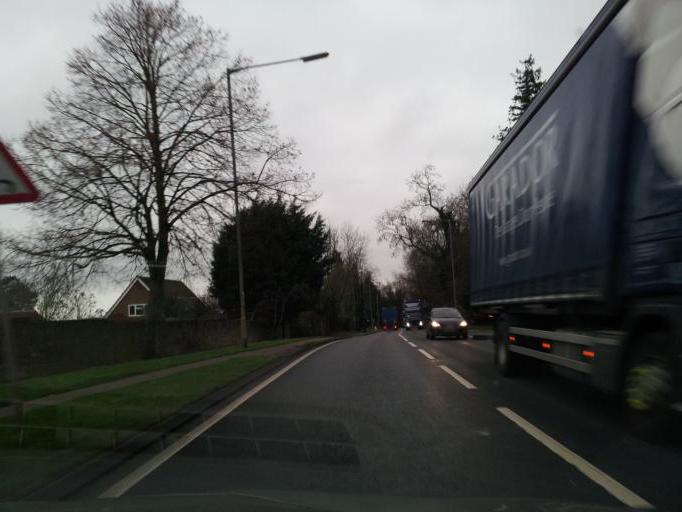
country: GB
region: England
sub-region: Northamptonshire
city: Daventry
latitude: 52.3359
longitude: -1.1735
